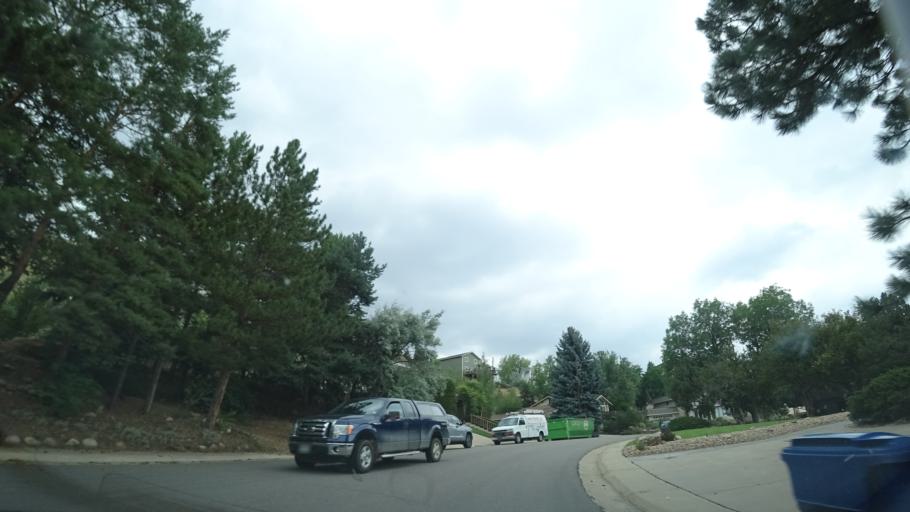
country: US
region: Colorado
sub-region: Jefferson County
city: West Pleasant View
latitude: 39.6978
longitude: -105.1541
